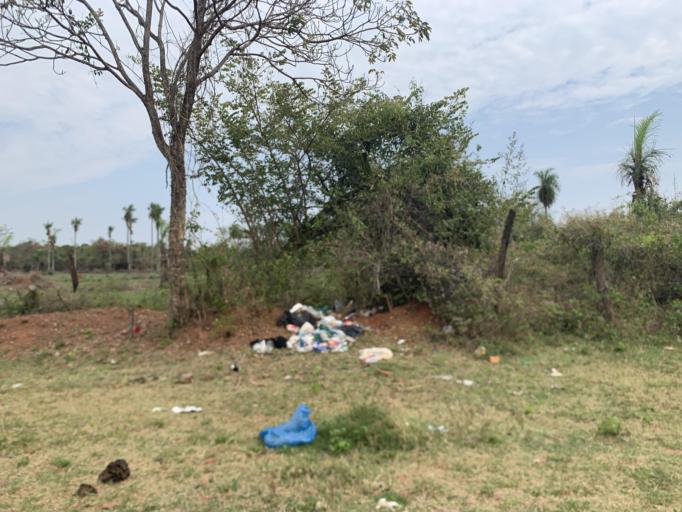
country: PY
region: Misiones
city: San Juan Bautista
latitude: -26.6640
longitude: -57.1547
